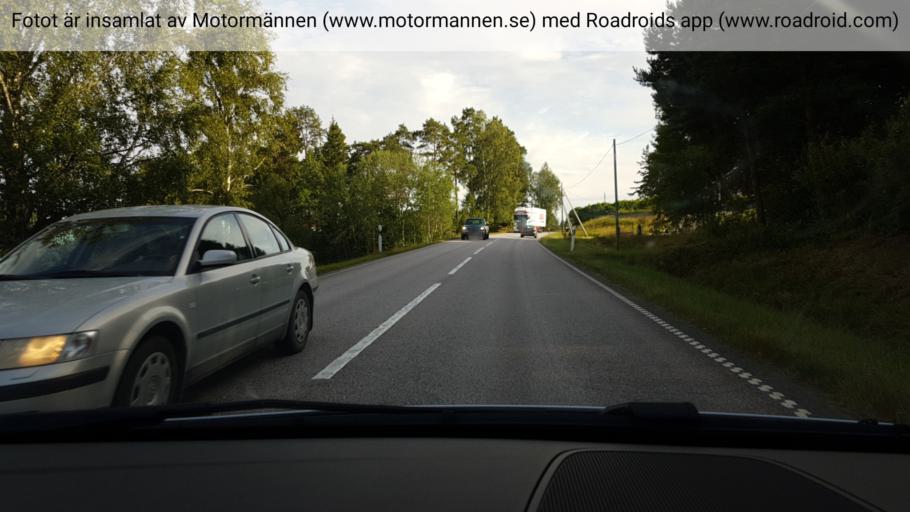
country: SE
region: Stockholm
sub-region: Norrtalje Kommun
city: Norrtalje
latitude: 59.8764
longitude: 18.7003
